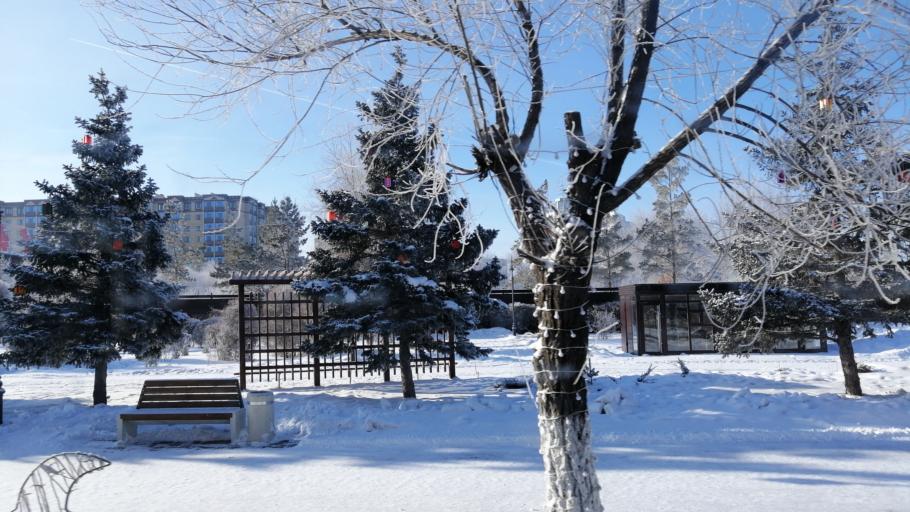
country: KZ
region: Aqtoebe
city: Aqtobe
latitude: 50.2932
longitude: 57.1597
